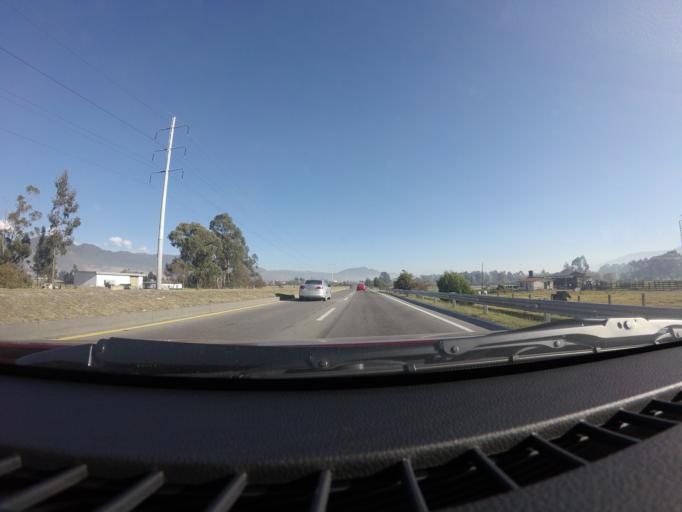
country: CO
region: Cundinamarca
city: Zipaquira
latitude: 5.0040
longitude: -73.9895
